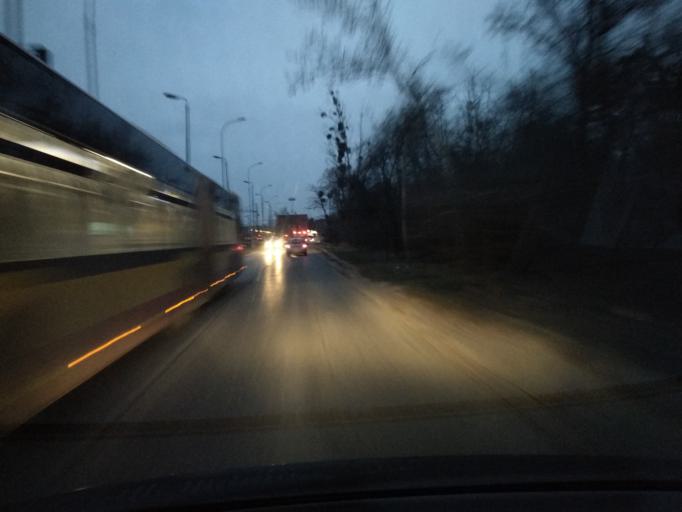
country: PL
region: Lower Silesian Voivodeship
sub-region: Powiat wroclawski
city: Wroclaw
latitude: 51.1253
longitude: 16.9563
